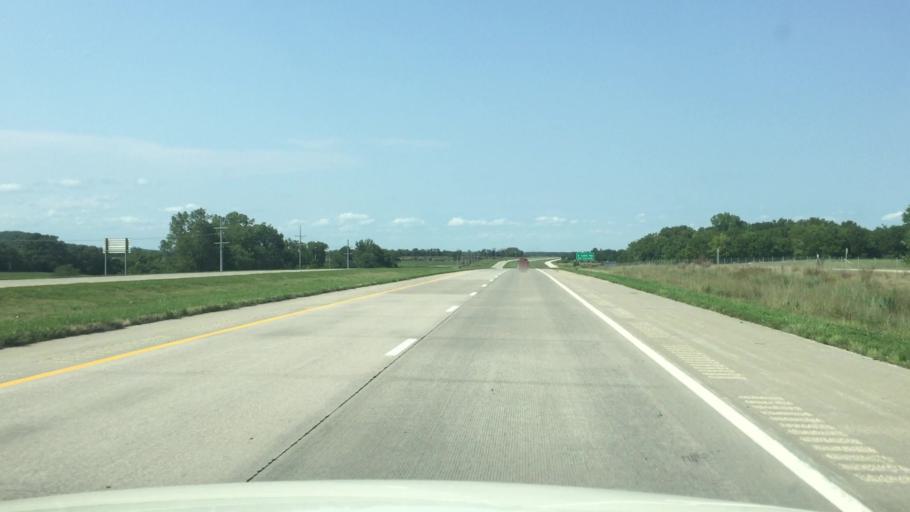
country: US
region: Kansas
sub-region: Linn County
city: Pleasanton
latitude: 38.1960
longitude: -94.7054
